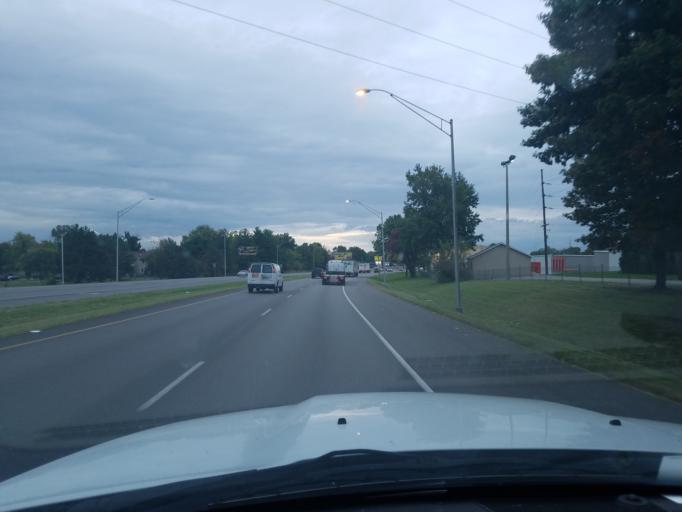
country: US
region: Indiana
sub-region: Vanderburgh County
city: Evansville
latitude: 37.9551
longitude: -87.5424
